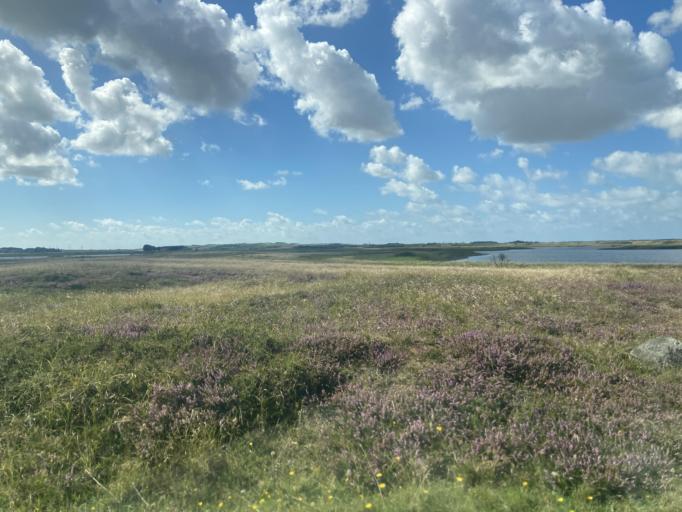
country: DK
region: Central Jutland
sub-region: Lemvig Kommune
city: Lemvig
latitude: 56.5972
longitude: 8.2874
